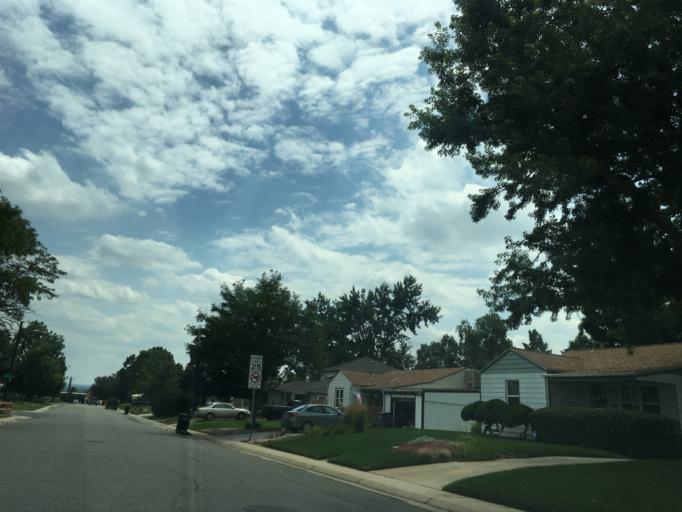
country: US
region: Colorado
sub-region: Arapahoe County
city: Sheridan
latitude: 39.6650
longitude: -105.0298
